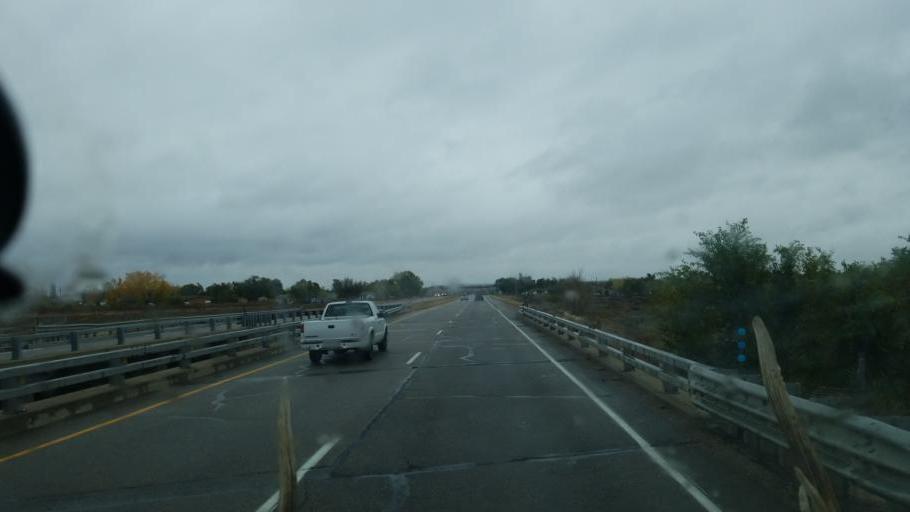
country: US
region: Colorado
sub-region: Pueblo County
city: Pueblo
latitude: 38.2804
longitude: -104.5684
